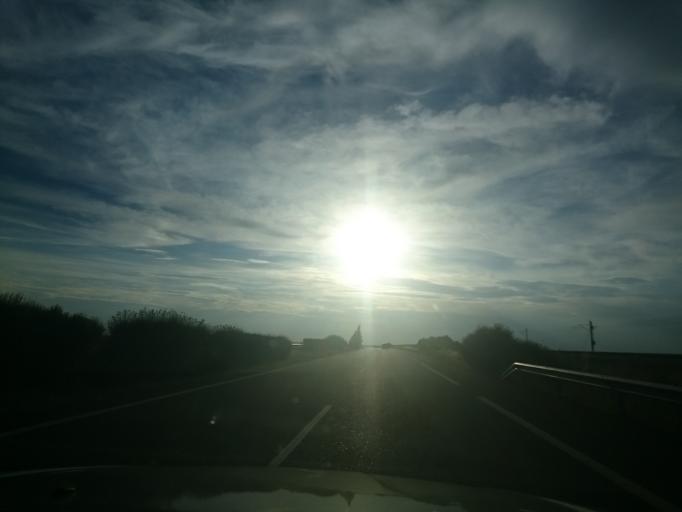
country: ES
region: Castille and Leon
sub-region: Provincia de Leon
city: Villamoratiel de las Matas
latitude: 42.4196
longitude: -5.2371
